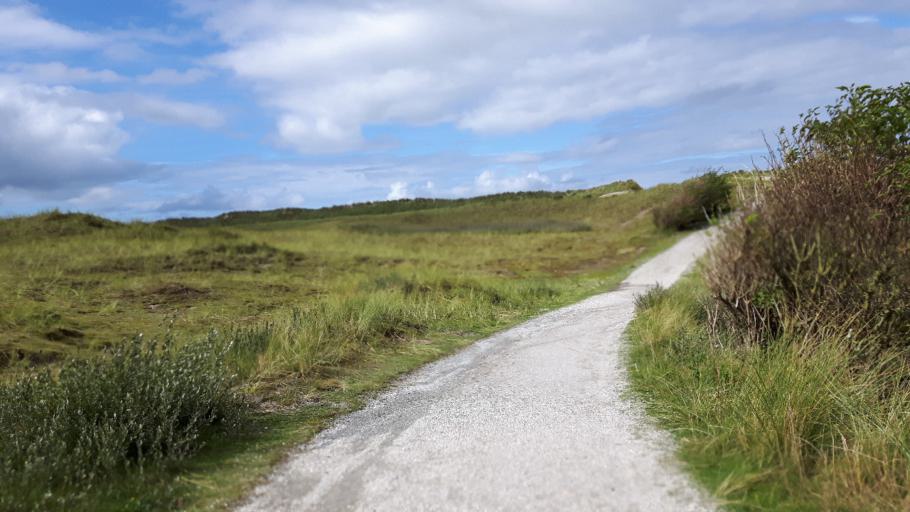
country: NL
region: Friesland
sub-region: Gemeente Ameland
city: Hollum
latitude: 53.4523
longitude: 5.6202
